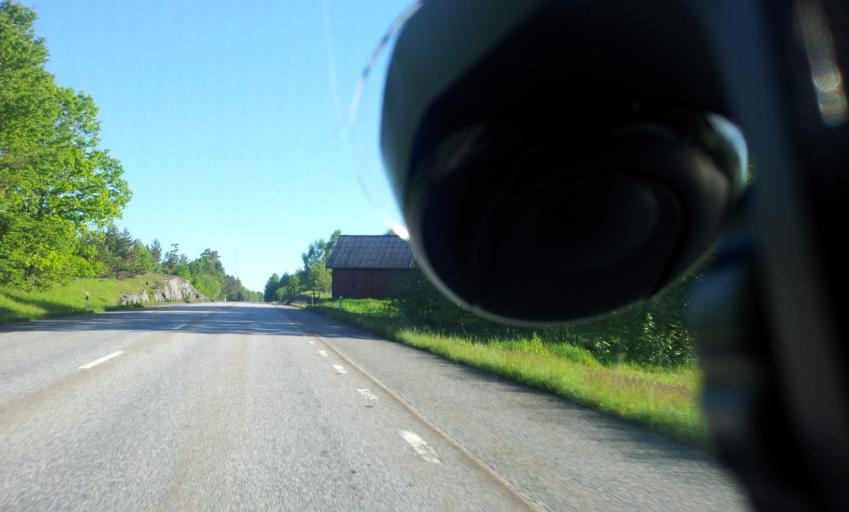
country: SE
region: Kalmar
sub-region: Vasterviks Kommun
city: Ankarsrum
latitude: 57.6814
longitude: 16.4430
